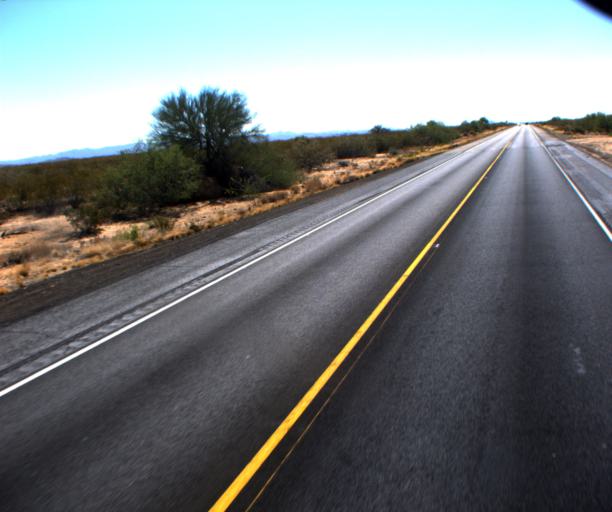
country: US
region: Arizona
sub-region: Yavapai County
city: Congress
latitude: 34.0525
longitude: -112.8487
